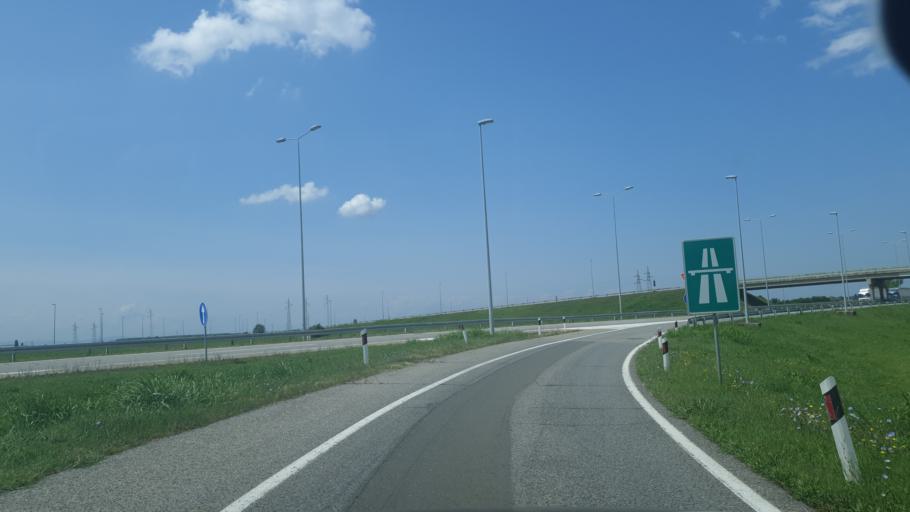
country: RS
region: Autonomna Pokrajina Vojvodina
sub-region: Sremski Okrug
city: Sremska Mitrovica
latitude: 44.9992
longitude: 19.6529
